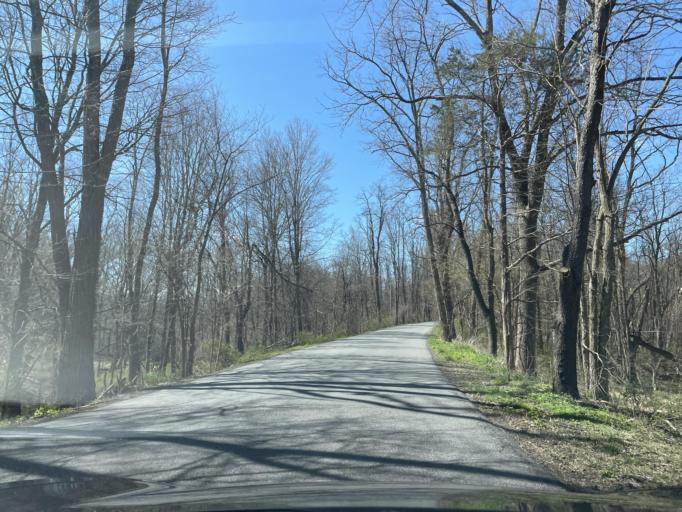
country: US
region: New York
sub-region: Ulster County
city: Saugerties South
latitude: 42.0515
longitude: -73.9925
